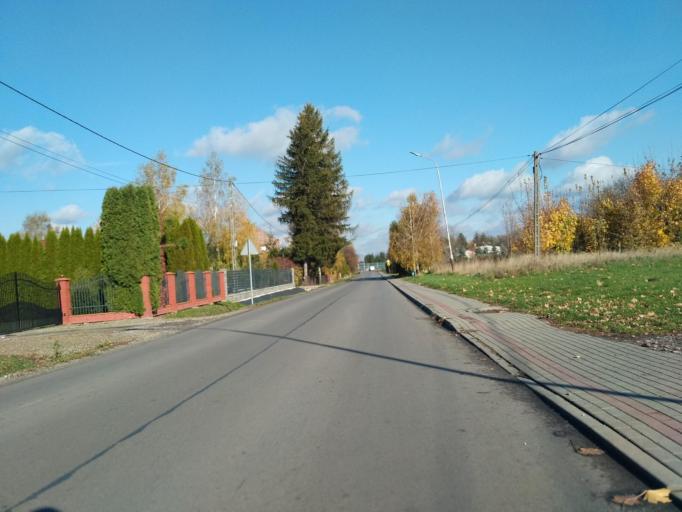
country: PL
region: Subcarpathian Voivodeship
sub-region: Powiat rzeszowski
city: Trzciana
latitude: 50.0758
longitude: 21.8359
